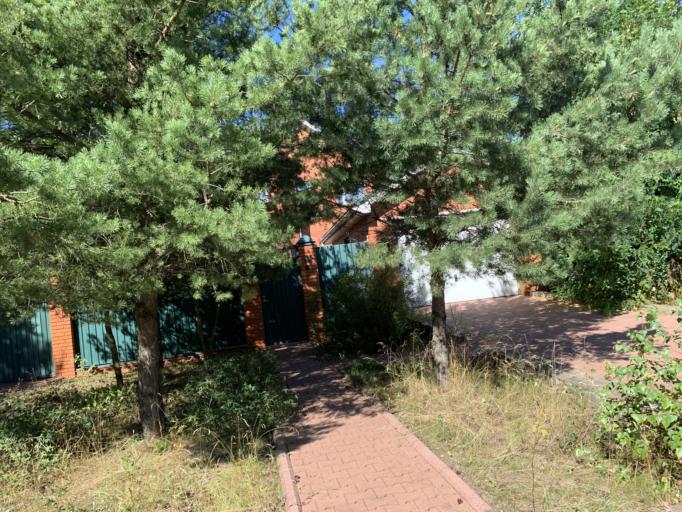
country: RU
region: Moskovskaya
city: Mamontovka
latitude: 55.9697
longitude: 37.8364
